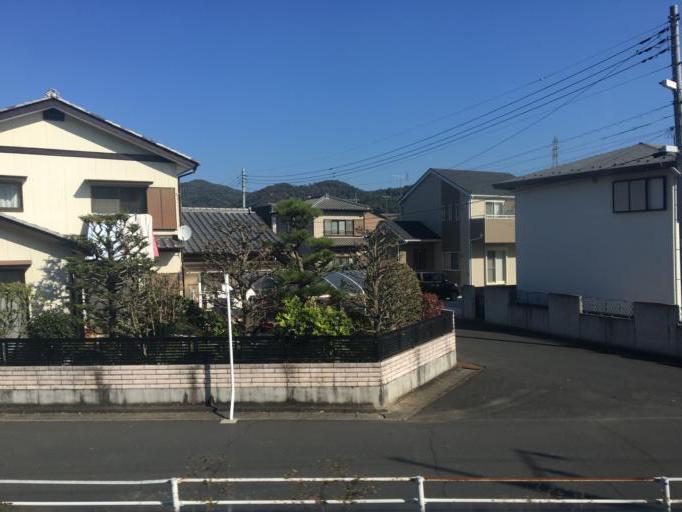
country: JP
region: Gunma
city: Kiryu
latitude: 36.3678
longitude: 139.3835
